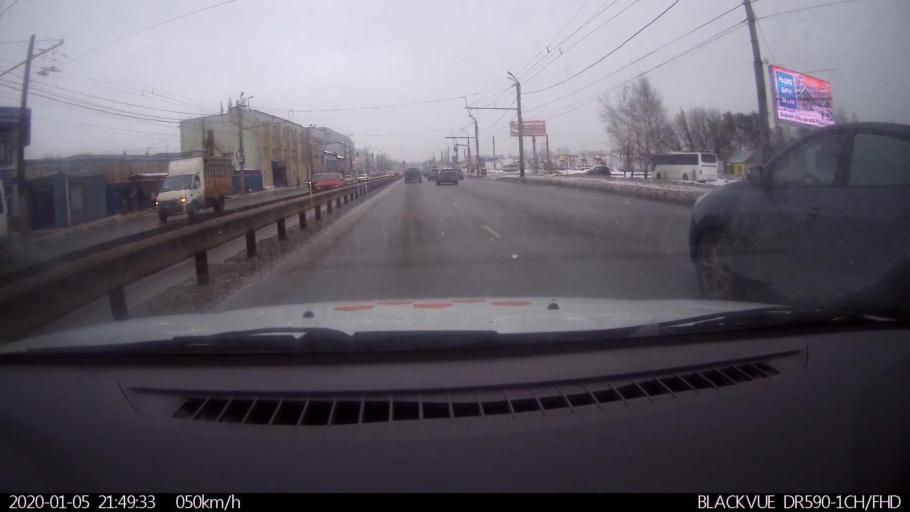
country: RU
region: Nizjnij Novgorod
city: Nizhniy Novgorod
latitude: 56.3050
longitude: 43.8757
